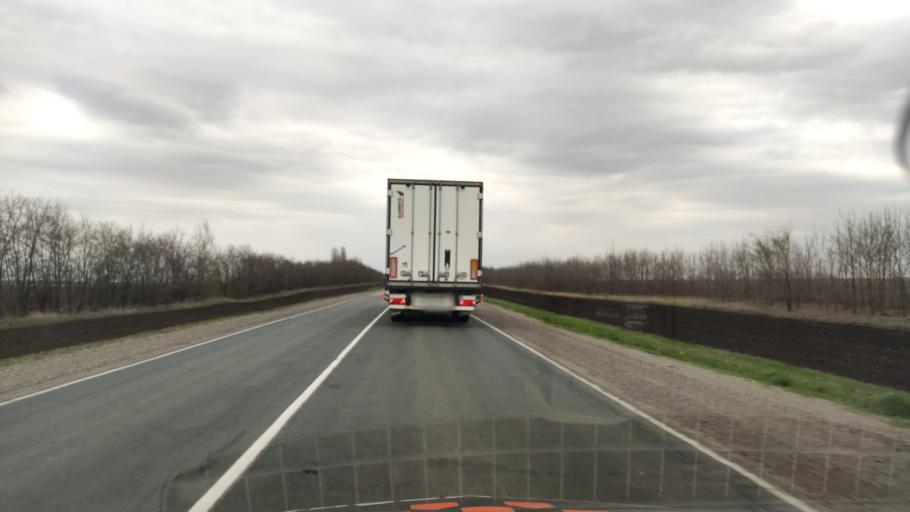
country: RU
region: Voronezj
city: Nizhnedevitsk
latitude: 51.5730
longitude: 38.3298
